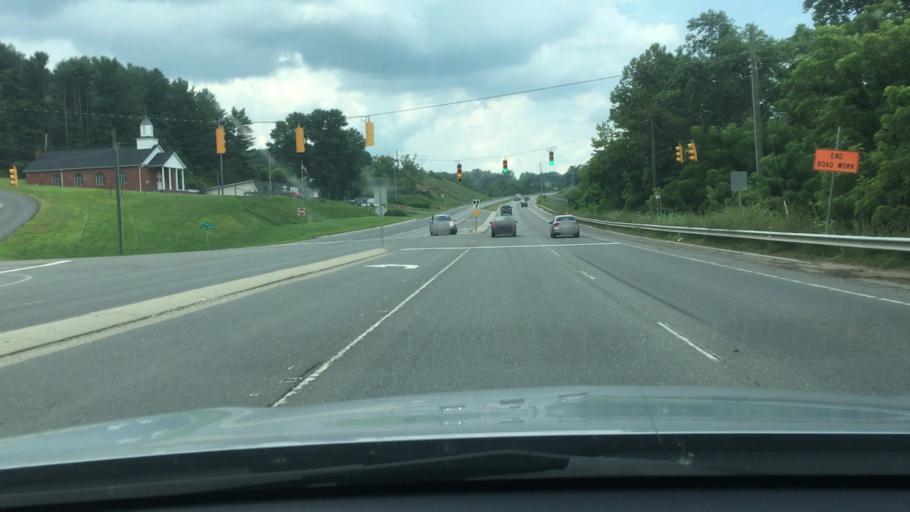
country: US
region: North Carolina
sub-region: Yancey County
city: Burnsville
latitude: 35.9118
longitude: -82.3481
